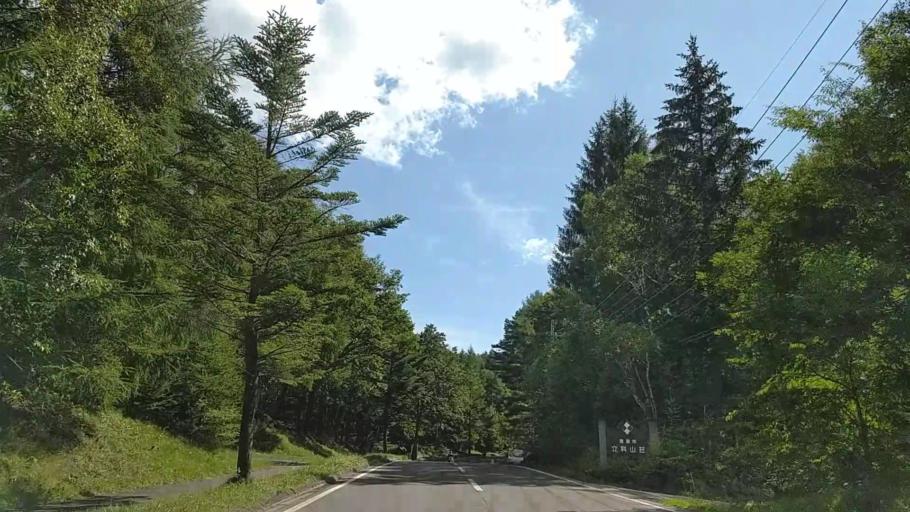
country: JP
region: Nagano
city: Chino
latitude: 36.1251
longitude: 138.2680
